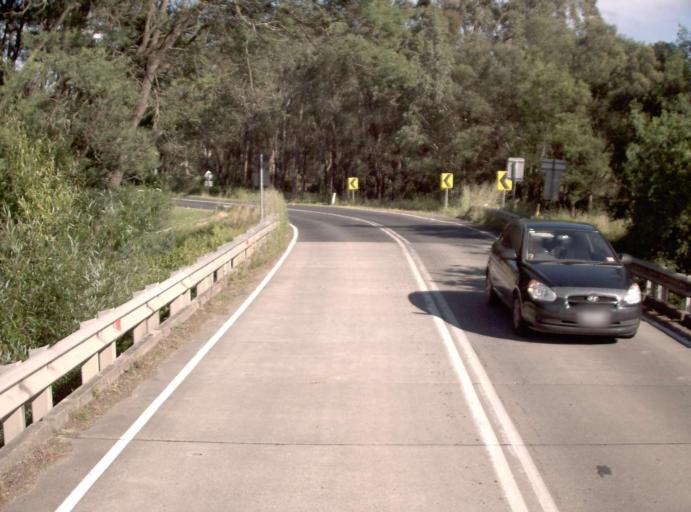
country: AU
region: Victoria
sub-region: Latrobe
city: Traralgon
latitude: -38.1736
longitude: 146.4966
